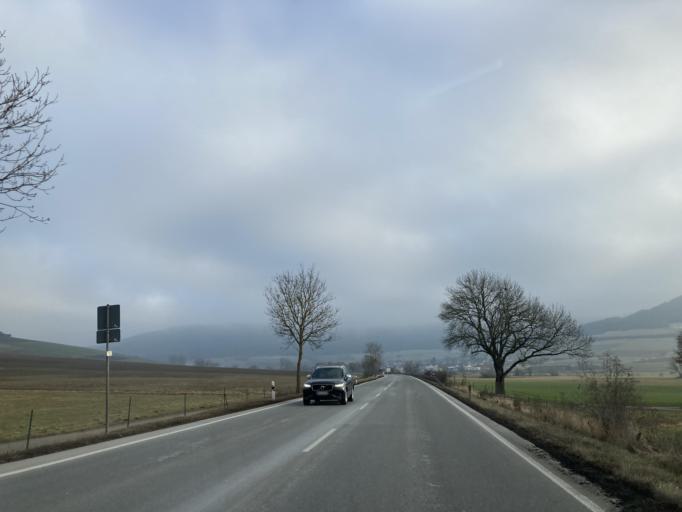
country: DE
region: Baden-Wuerttemberg
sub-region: Freiburg Region
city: Geisingen
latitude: 47.9225
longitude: 8.5976
